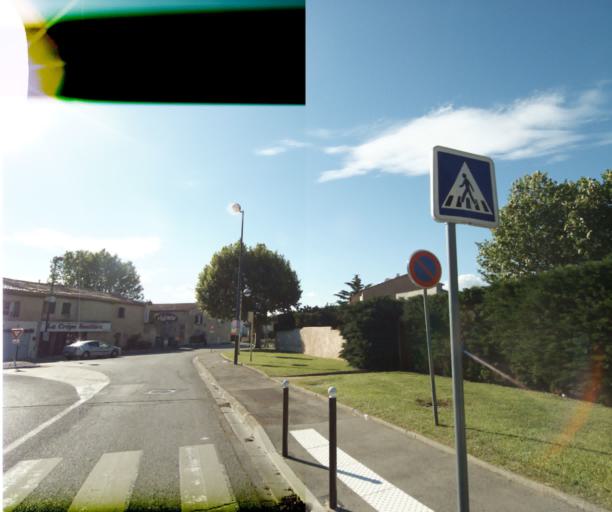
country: FR
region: Provence-Alpes-Cote d'Azur
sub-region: Departement des Bouches-du-Rhone
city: Rognac
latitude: 43.4883
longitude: 5.2215
